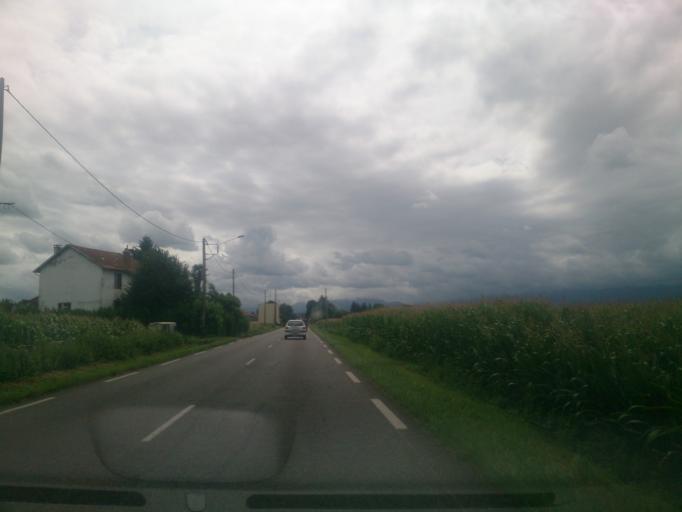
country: FR
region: Midi-Pyrenees
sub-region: Departement des Hautes-Pyrenees
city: Laloubere
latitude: 43.1978
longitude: 0.0786
